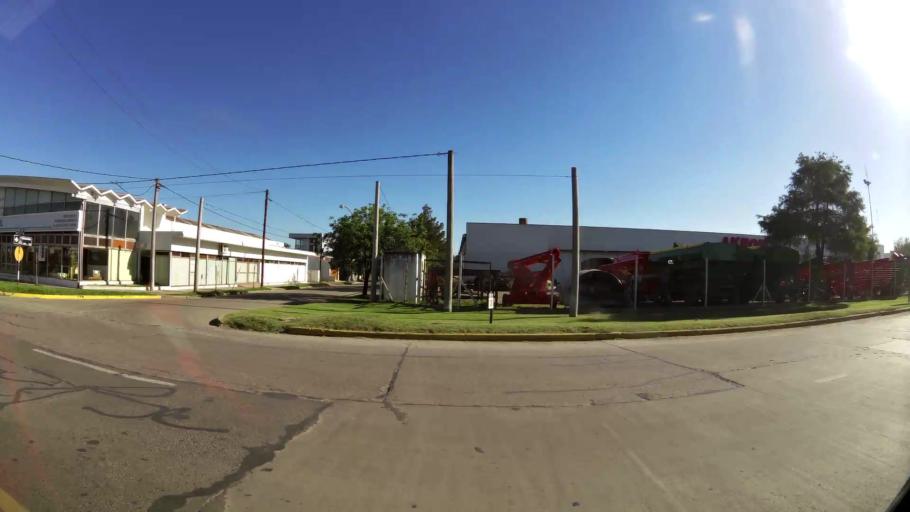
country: AR
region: Cordoba
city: San Francisco
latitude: -31.4151
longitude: -62.0923
